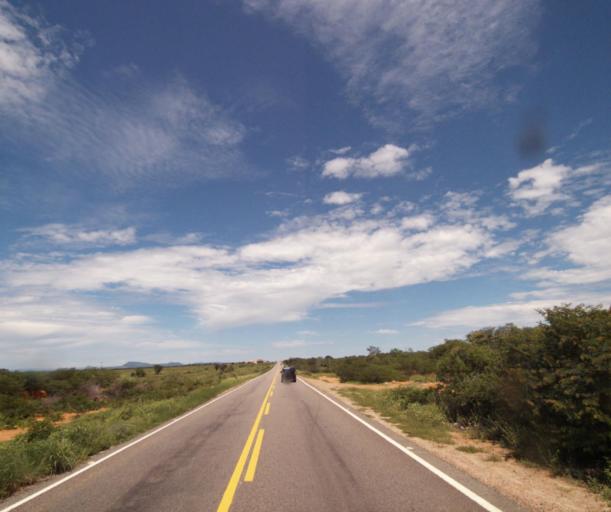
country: BR
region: Bahia
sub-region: Palmas De Monte Alto
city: Palmas de Monte Alto
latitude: -14.2481
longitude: -43.1450
